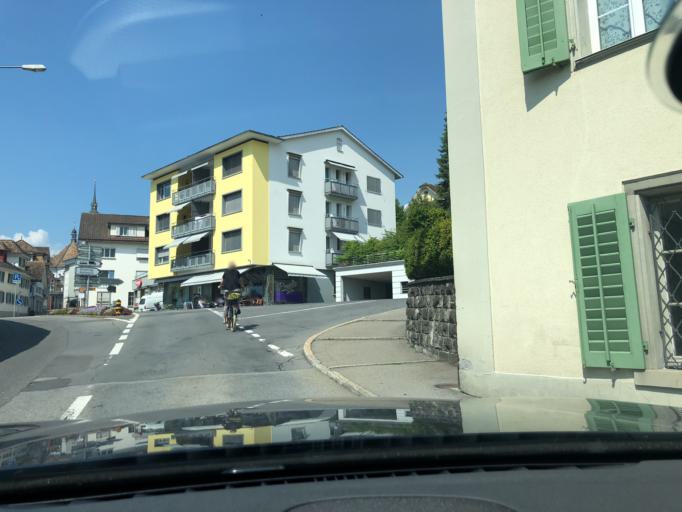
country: CH
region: Schwyz
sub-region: Bezirk Schwyz
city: Schwyz
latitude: 47.0204
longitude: 8.6576
